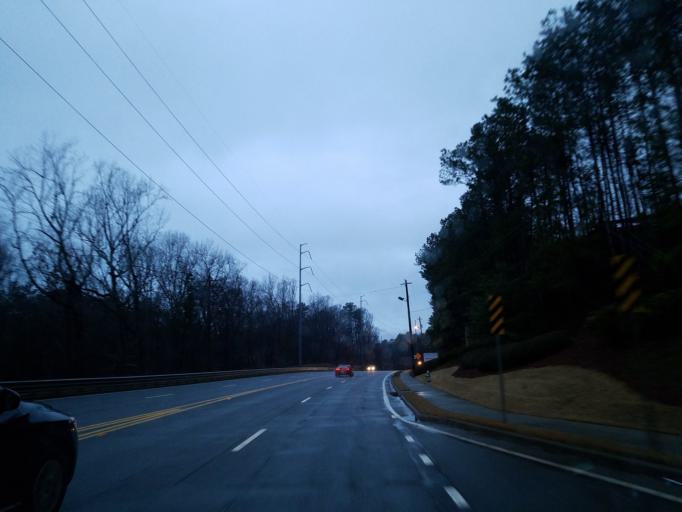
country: US
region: Georgia
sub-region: Fulton County
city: Roswell
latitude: 34.0086
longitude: -84.3000
